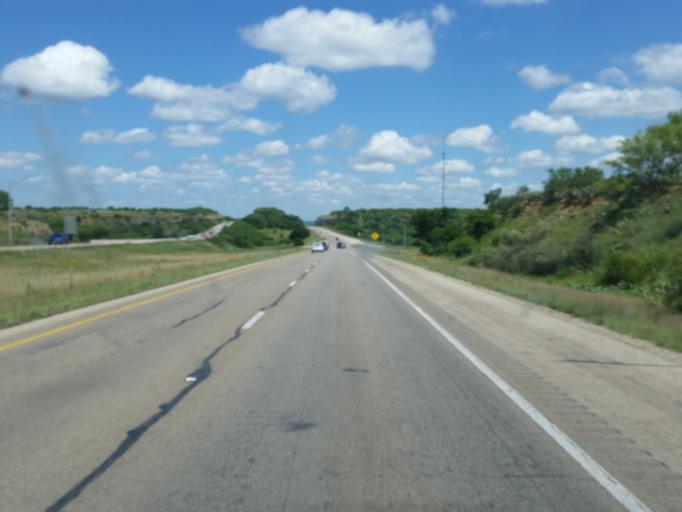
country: US
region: Texas
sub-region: Callahan County
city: Baird
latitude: 32.3975
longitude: -99.3713
